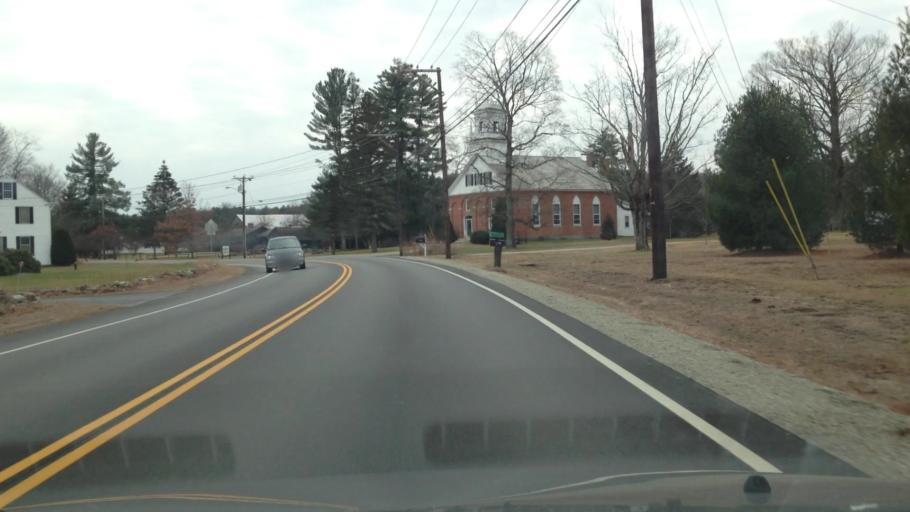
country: US
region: New Hampshire
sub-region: Cheshire County
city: Swanzey
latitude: 42.8699
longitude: -72.2826
